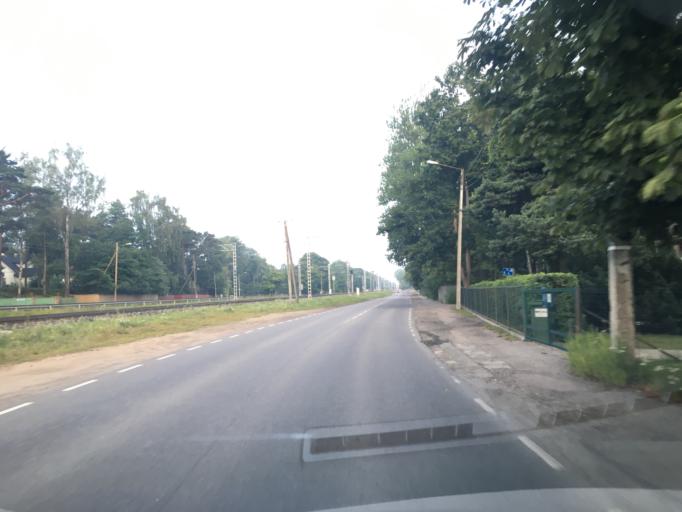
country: EE
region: Harju
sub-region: Tallinna linn
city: Tallinn
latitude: 59.3882
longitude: 24.6989
